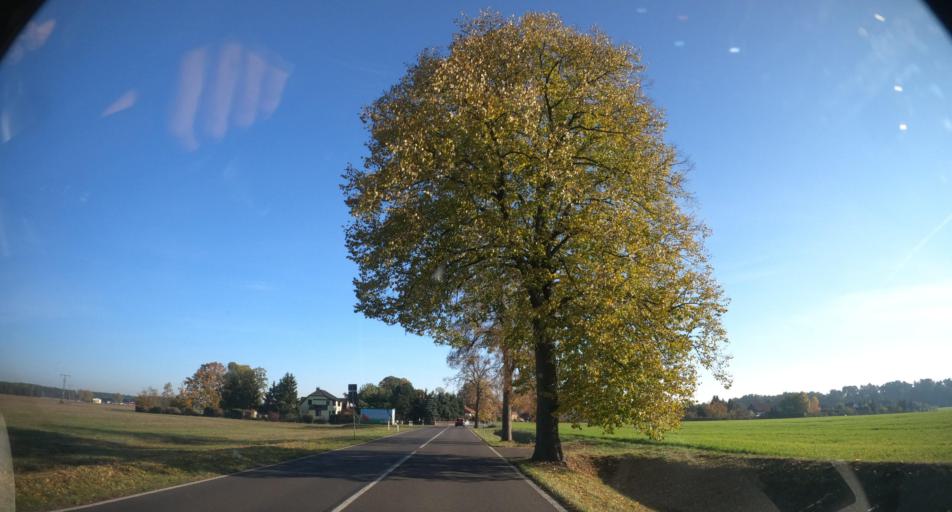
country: DE
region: Mecklenburg-Vorpommern
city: Ahlbeck
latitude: 53.6729
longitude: 14.1778
